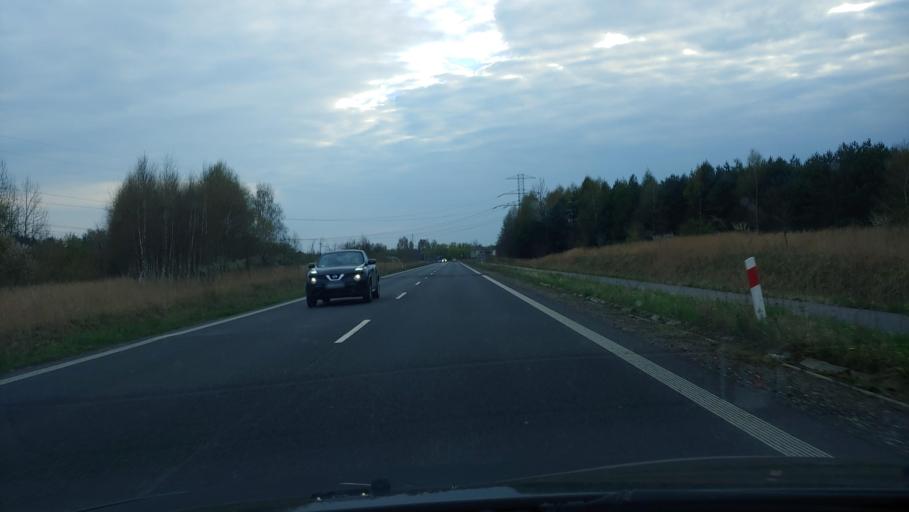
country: PL
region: Silesian Voivodeship
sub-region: Jaworzno
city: Jaworzno
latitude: 50.1617
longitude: 19.2758
